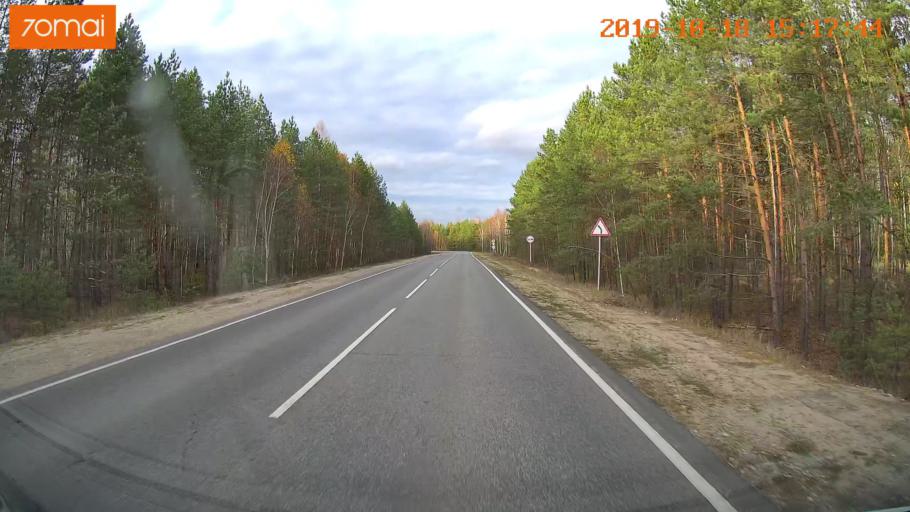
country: RU
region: Vladimir
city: Anopino
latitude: 55.6542
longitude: 40.7273
